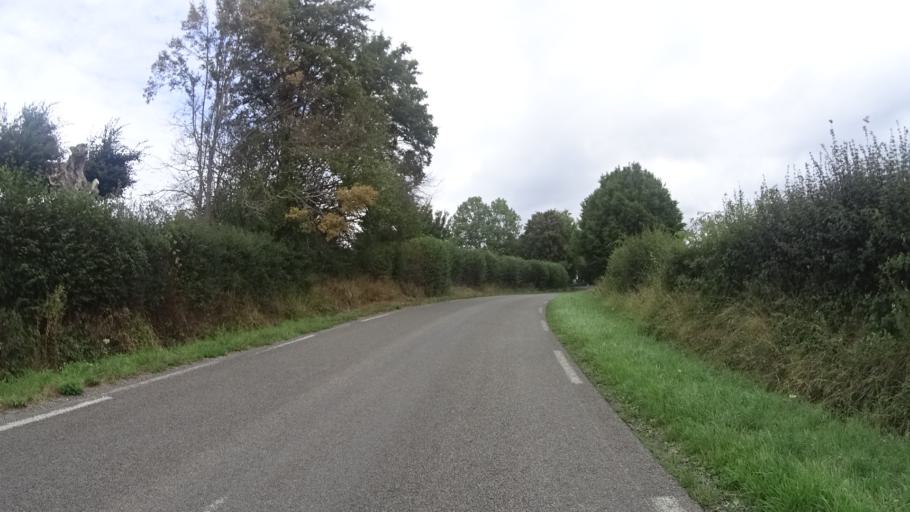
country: FR
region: Nord-Pas-de-Calais
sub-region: Departement du Nord
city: Berlaimont
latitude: 50.1898
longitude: 3.8072
